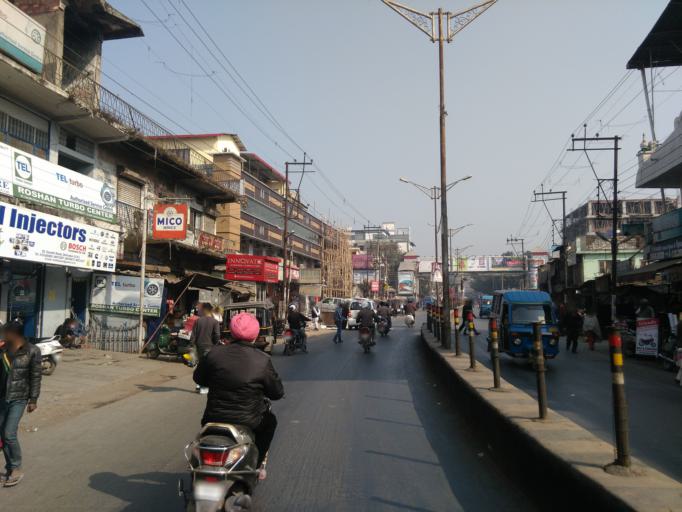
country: IN
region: Uttarakhand
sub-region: Dehradun
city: Dehradun
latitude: 30.3200
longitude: 78.0403
